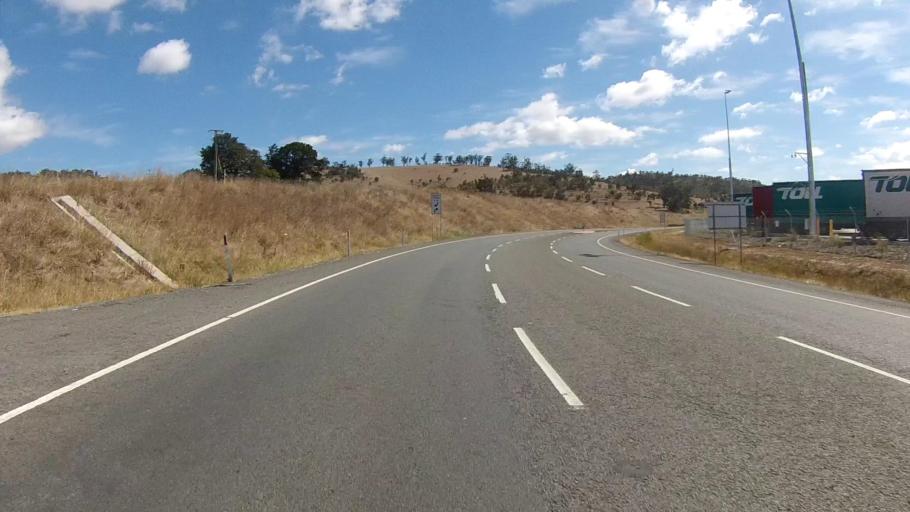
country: AU
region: Tasmania
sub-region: Brighton
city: Bridgewater
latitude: -42.7181
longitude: 147.2256
